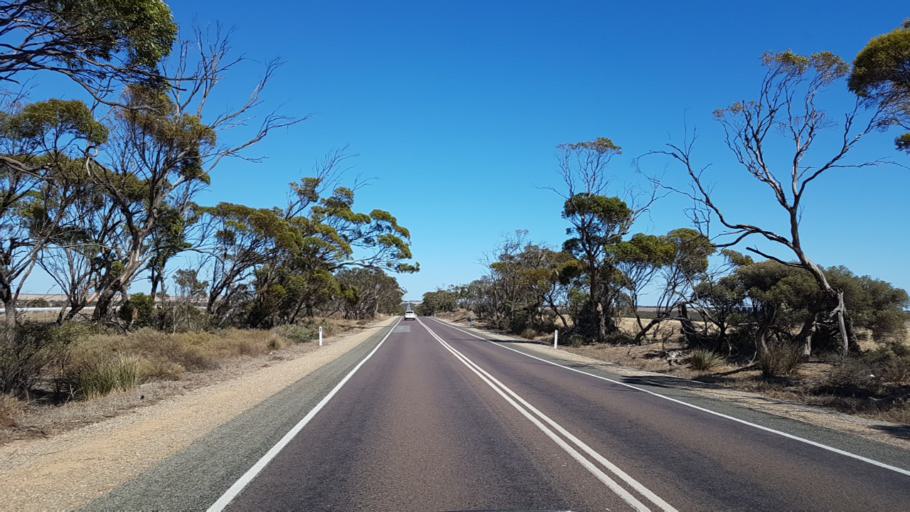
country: AU
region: South Australia
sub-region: Copper Coast
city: Kadina
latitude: -34.0536
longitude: 137.9984
